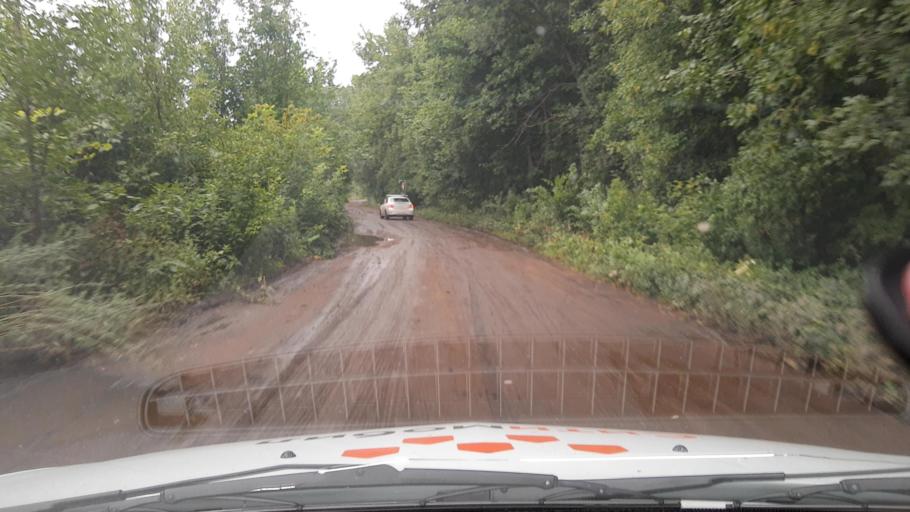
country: RU
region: Bashkortostan
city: Ufa
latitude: 54.5666
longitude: 55.9536
